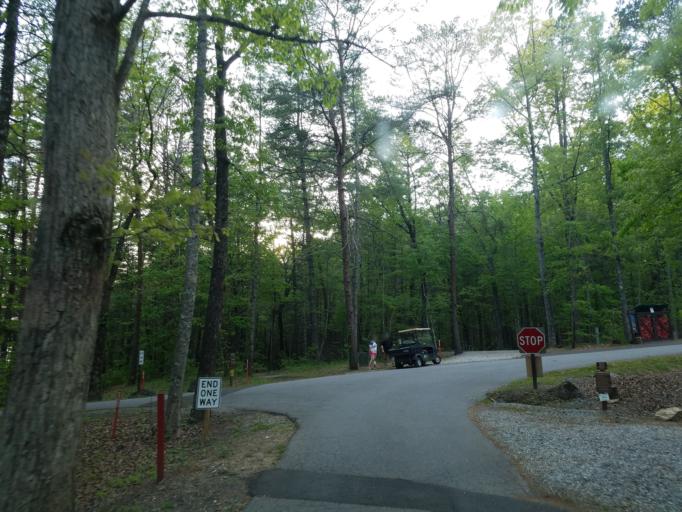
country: US
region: Georgia
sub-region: Fannin County
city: Blue Ridge
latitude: 34.8686
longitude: -84.2491
